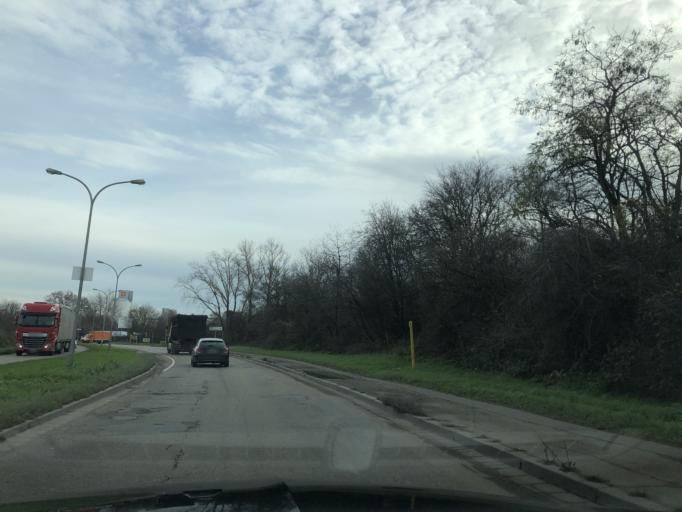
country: DE
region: Baden-Wuerttemberg
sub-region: Karlsruhe Region
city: Mannheim
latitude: 49.5206
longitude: 8.4556
